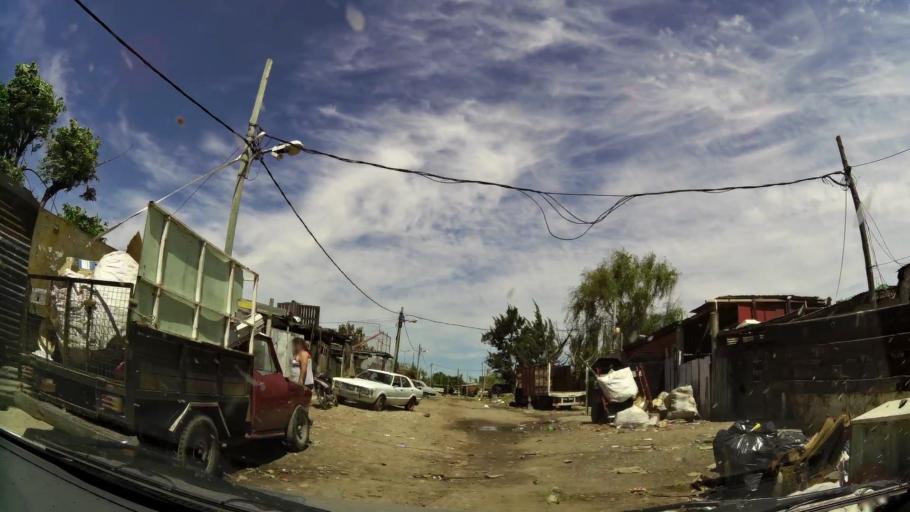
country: AR
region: Buenos Aires
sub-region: Partido de Quilmes
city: Quilmes
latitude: -34.7429
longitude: -58.3074
